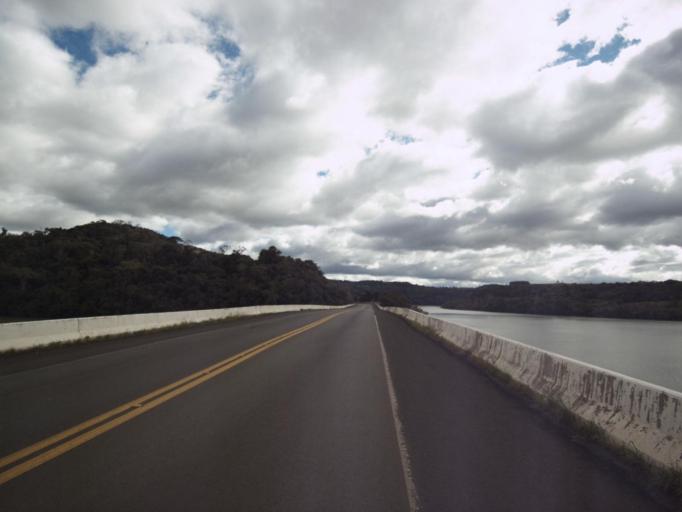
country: BR
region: Santa Catarina
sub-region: Concordia
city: Concordia
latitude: -27.3761
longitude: -51.9864
